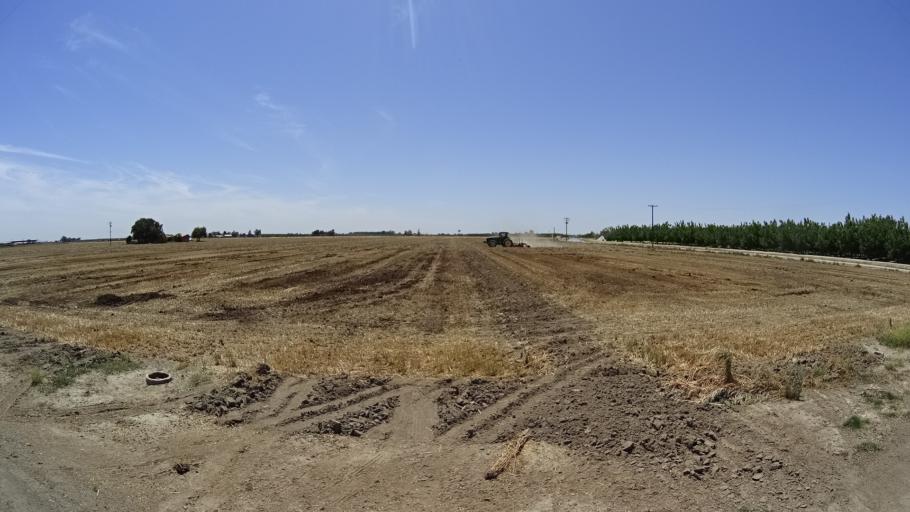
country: US
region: California
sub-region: Kings County
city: Lemoore
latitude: 36.3390
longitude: -119.7592
